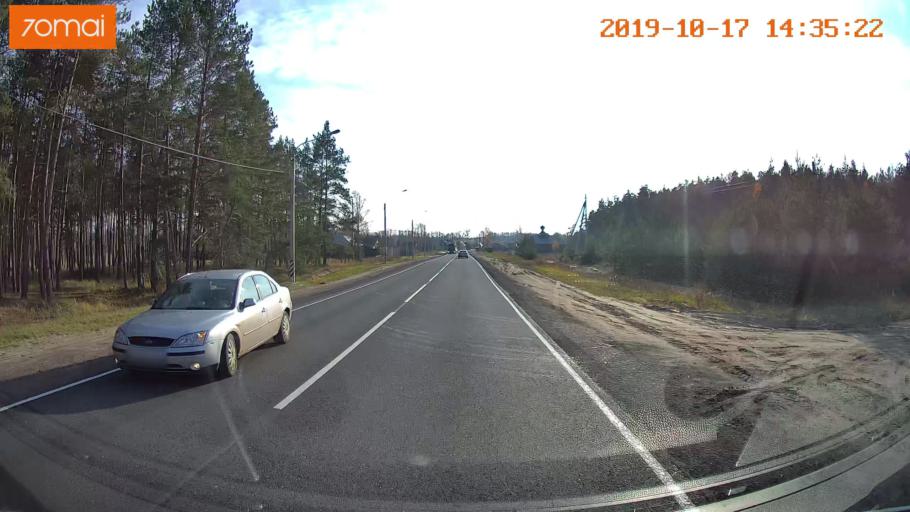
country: RU
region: Rjazan
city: Solotcha
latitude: 54.9007
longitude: 40.0026
